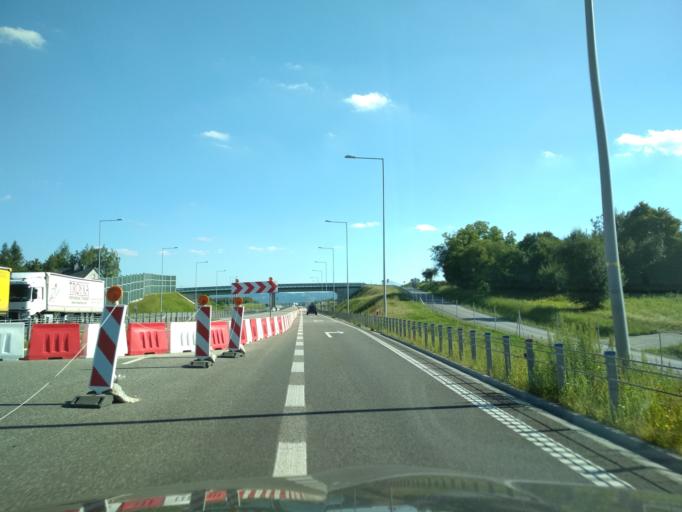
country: PL
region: Subcarpathian Voivodeship
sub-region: Powiat rzeszowski
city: Kielanowka
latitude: 50.0192
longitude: 21.9217
